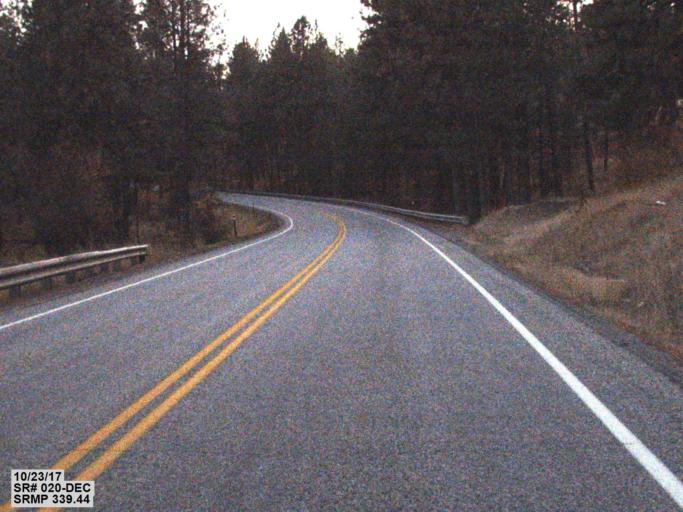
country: US
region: Washington
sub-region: Stevens County
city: Kettle Falls
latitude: 48.5949
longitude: -118.1458
